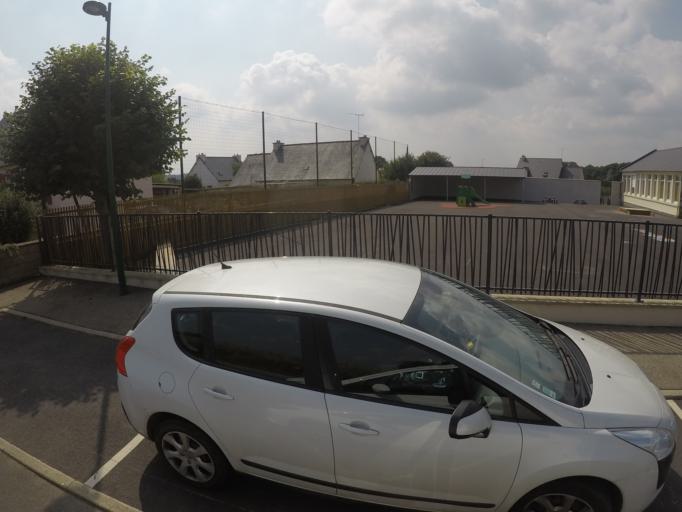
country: FR
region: Brittany
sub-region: Departement des Cotes-d'Armor
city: Saint-Donan
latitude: 48.5045
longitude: -2.9135
